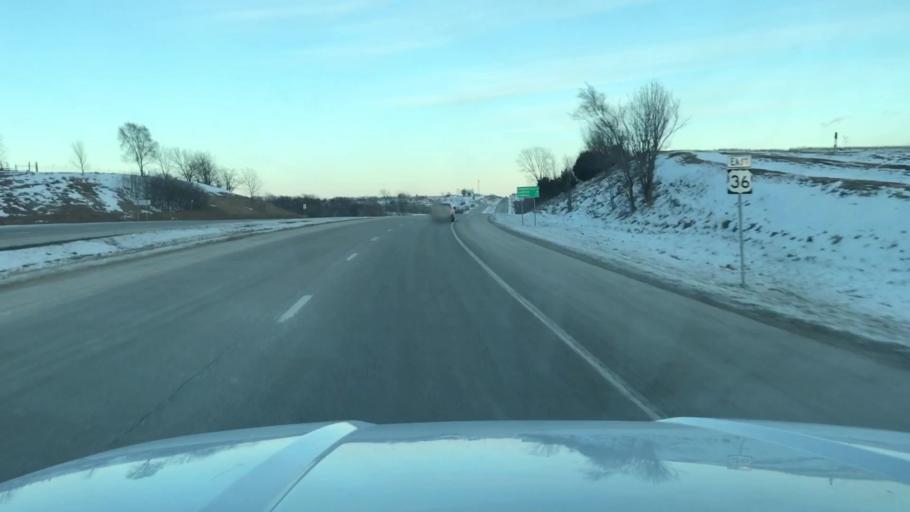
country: US
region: Missouri
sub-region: Clinton County
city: Gower
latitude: 39.7608
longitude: -94.5677
